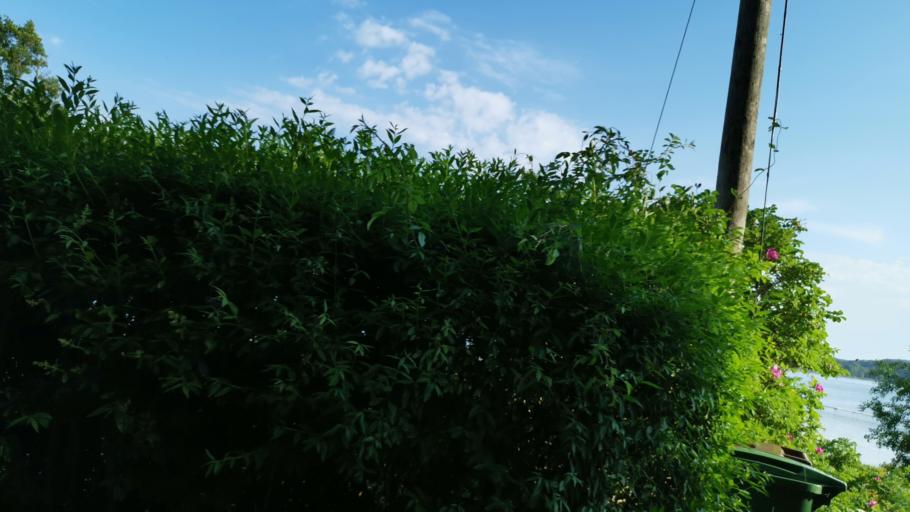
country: SE
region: Vaestra Goetaland
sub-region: Orust
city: Henan
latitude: 58.2852
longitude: 11.6620
